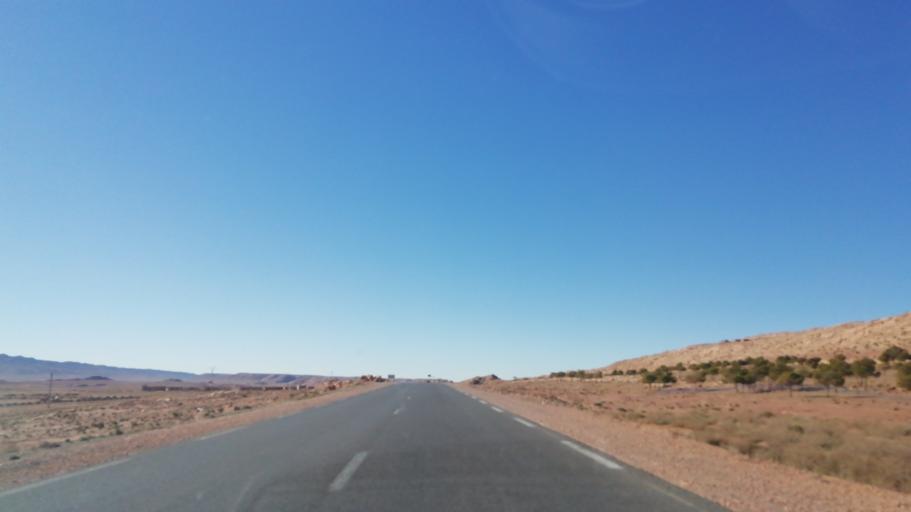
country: DZ
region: El Bayadh
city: El Bayadh
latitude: 33.6151
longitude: 1.1800
